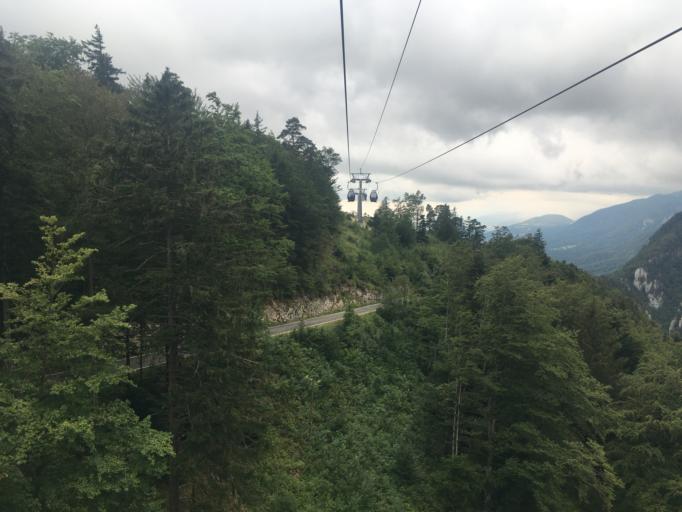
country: CH
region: Solothurn
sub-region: Bezirk Lebern
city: Langendorf
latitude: 47.2444
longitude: 7.5063
